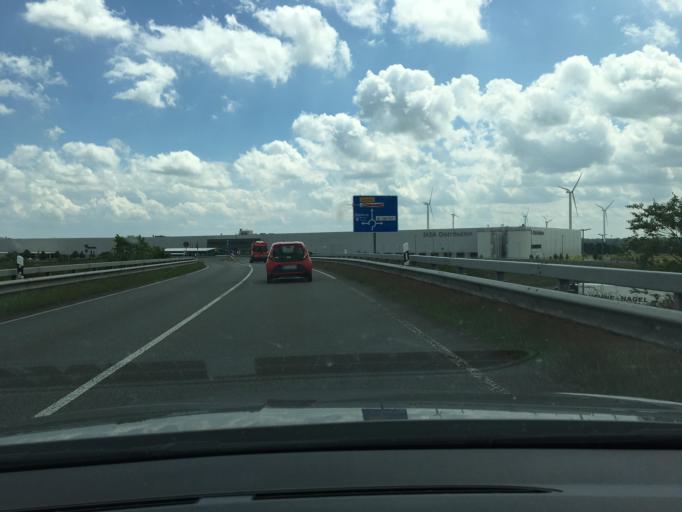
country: DE
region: Lower Saxony
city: Elsdorf
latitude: 53.2316
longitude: 9.3433
